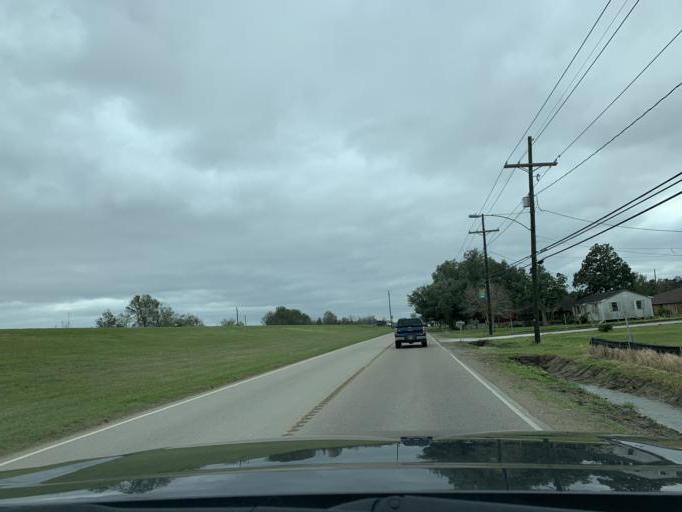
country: US
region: Louisiana
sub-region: Jefferson Parish
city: River Ridge
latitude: 29.9450
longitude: -90.2303
